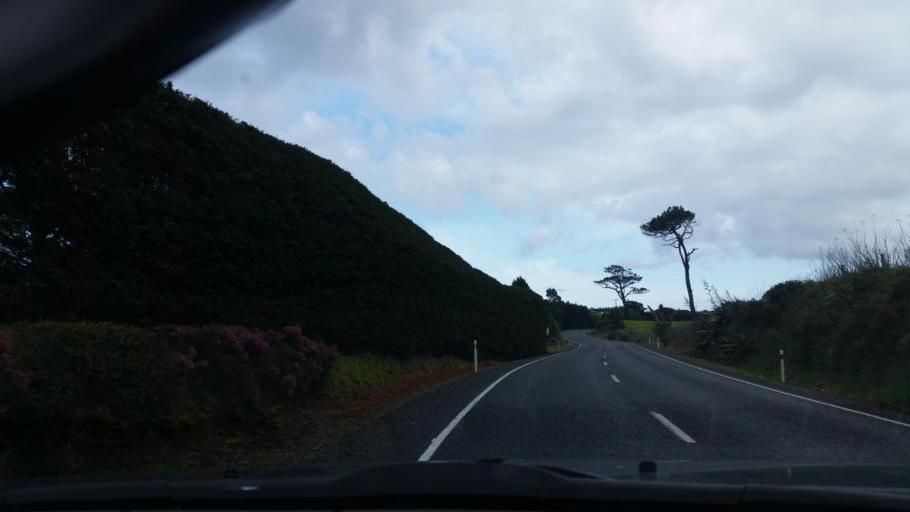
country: NZ
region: Northland
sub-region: Kaipara District
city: Dargaville
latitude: -35.9469
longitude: 173.7709
